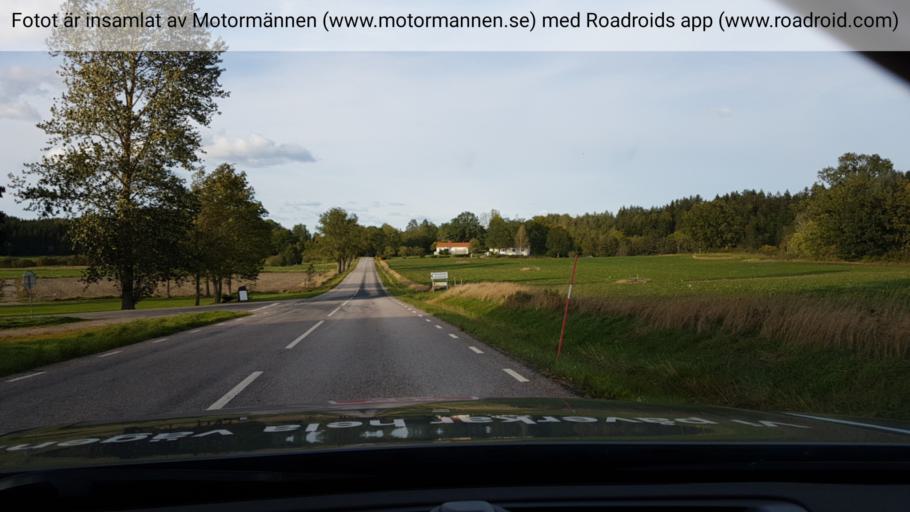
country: SE
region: Kalmar
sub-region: Vasterviks Kommun
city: Gamleby
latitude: 57.9129
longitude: 16.4117
